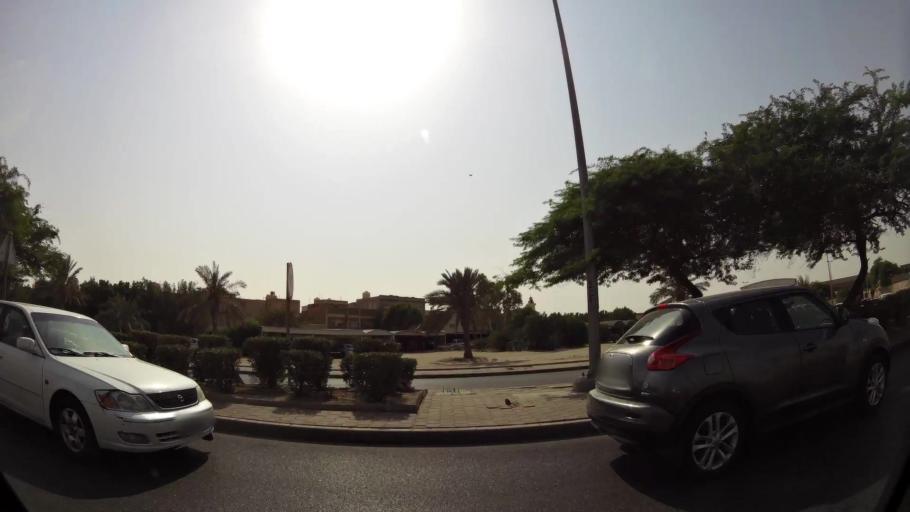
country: KW
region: Muhafazat al Jahra'
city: Al Jahra'
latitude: 29.3433
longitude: 47.6661
